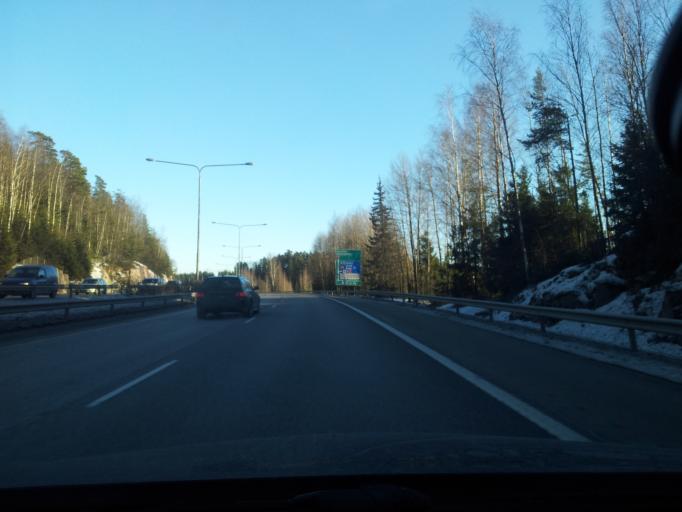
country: FI
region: Uusimaa
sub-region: Helsinki
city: Espoo
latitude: 60.2252
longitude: 24.6109
